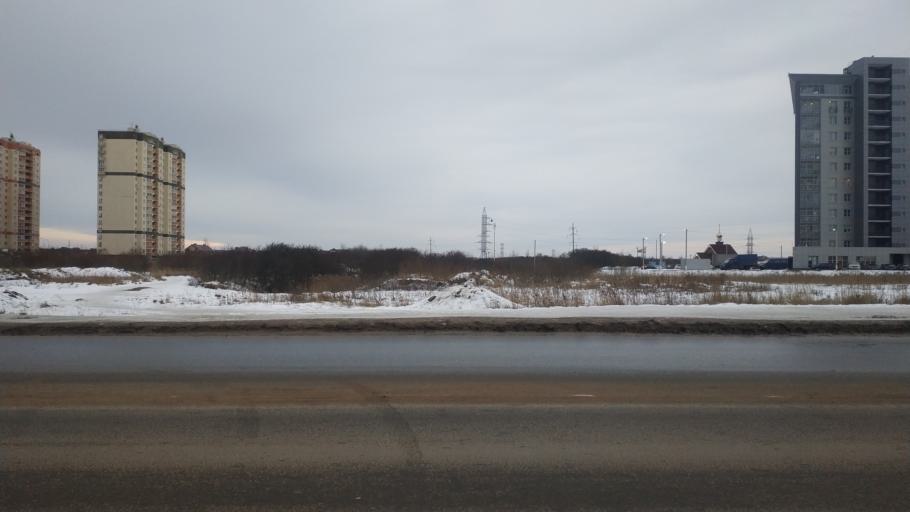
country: RU
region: Tverskaya
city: Tver
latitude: 56.8242
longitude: 35.8673
